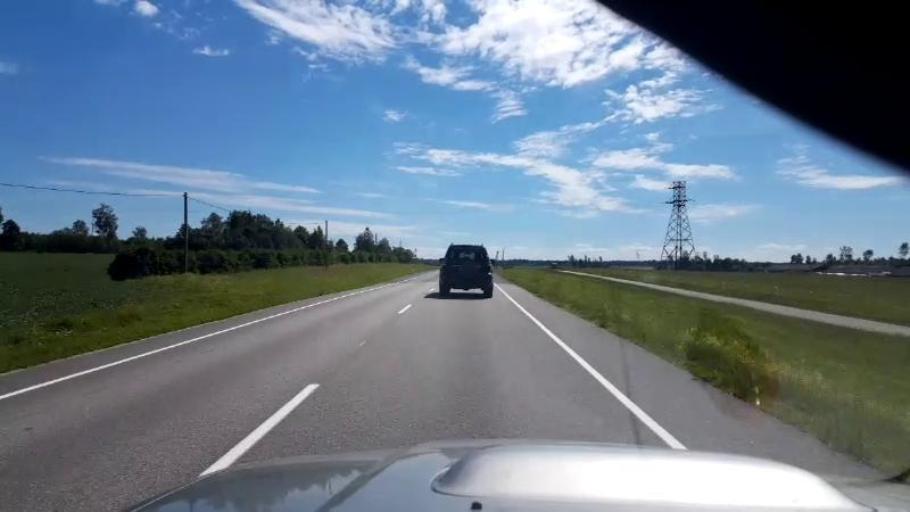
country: EE
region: Jaervamaa
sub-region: Jaerva-Jaani vald
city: Jarva-Jaani
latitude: 59.0264
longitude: 25.8969
